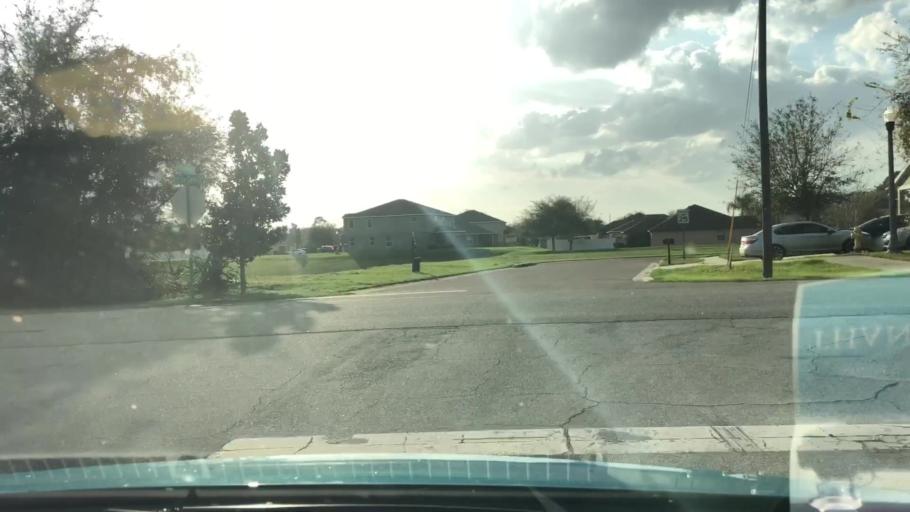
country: US
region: Florida
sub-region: Volusia County
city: Deltona
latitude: 28.8730
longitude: -81.2482
